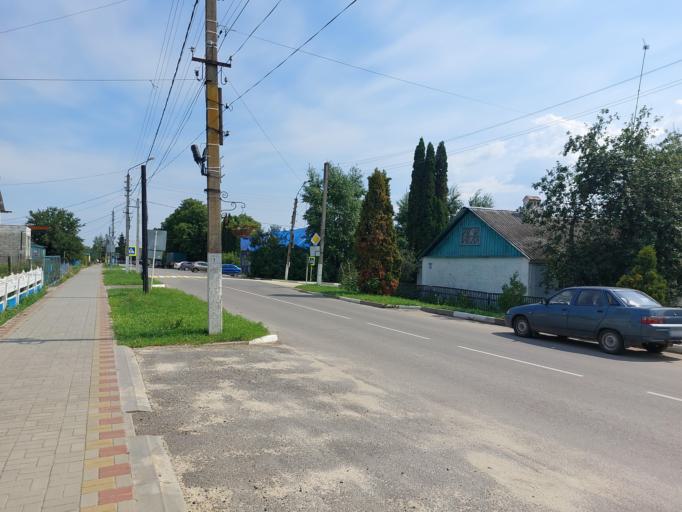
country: RU
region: Lipetsk
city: Dolgorukovo
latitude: 52.3243
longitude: 38.3595
